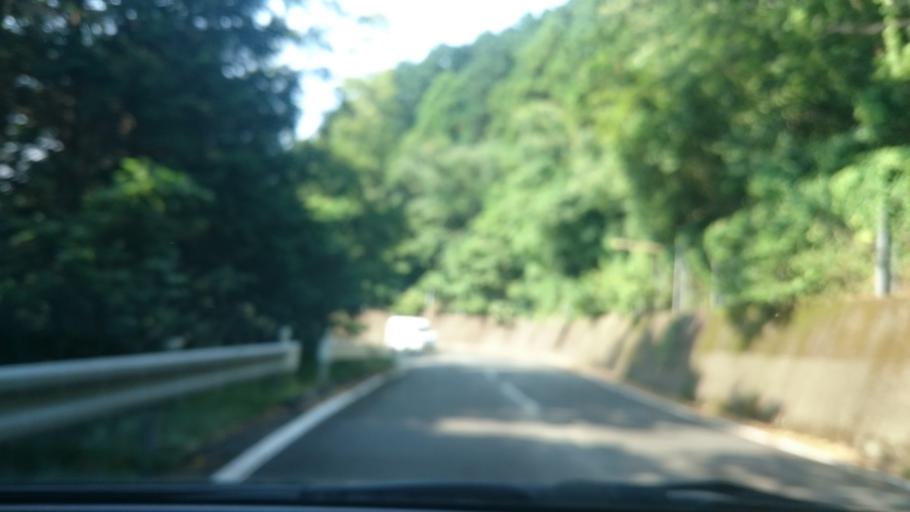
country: JP
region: Shizuoka
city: Heda
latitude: 34.9939
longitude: 138.7799
